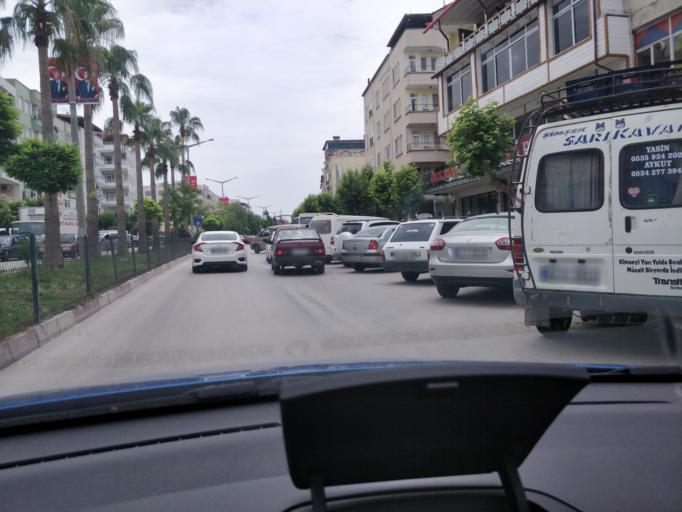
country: TR
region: Mersin
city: Mut
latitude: 36.6447
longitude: 33.4381
